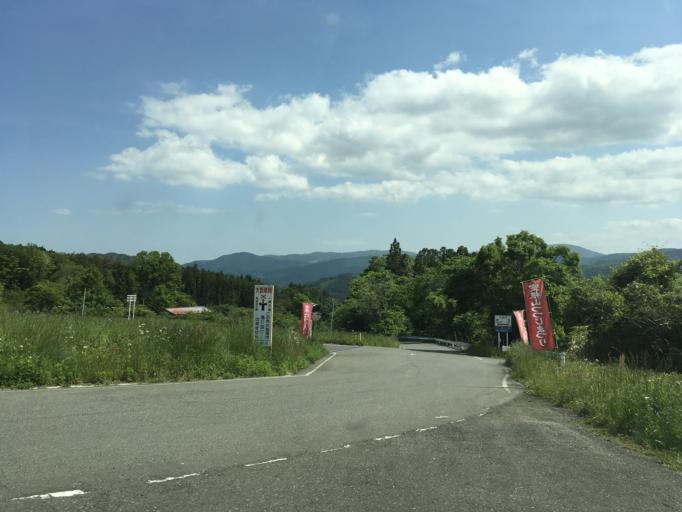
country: JP
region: Iwate
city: Ofunato
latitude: 38.9538
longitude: 141.4513
